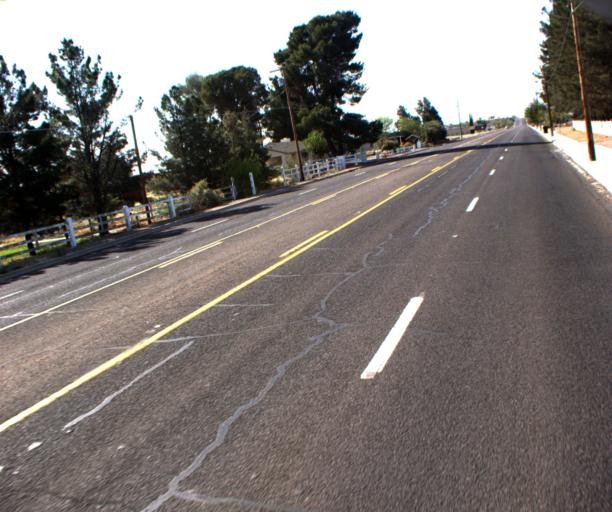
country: US
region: Arizona
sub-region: Graham County
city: Safford
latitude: 32.8155
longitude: -109.7077
